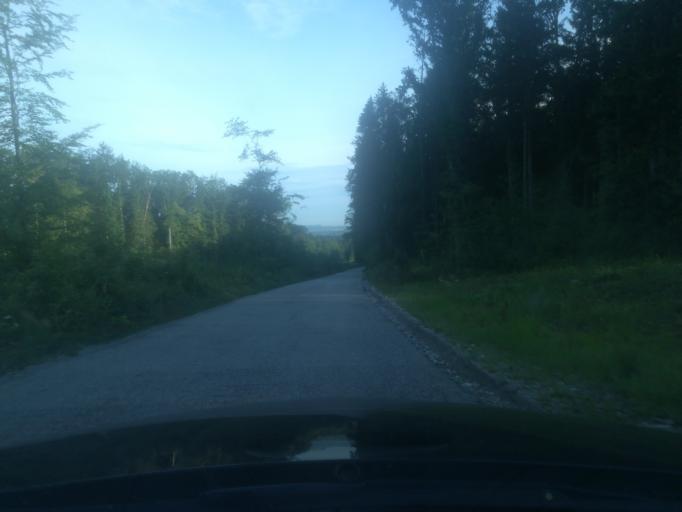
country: AT
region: Upper Austria
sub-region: Wels-Land
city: Marchtrenk
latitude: 48.1686
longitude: 14.1658
